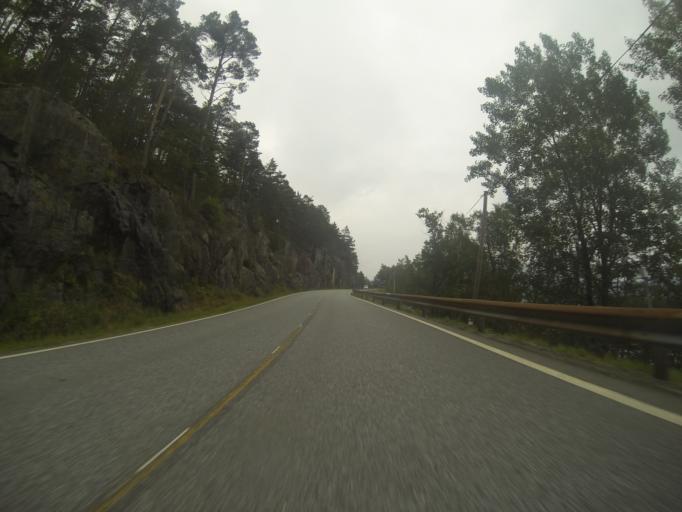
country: NO
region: Rogaland
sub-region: Suldal
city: Sand
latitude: 59.5212
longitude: 6.2447
